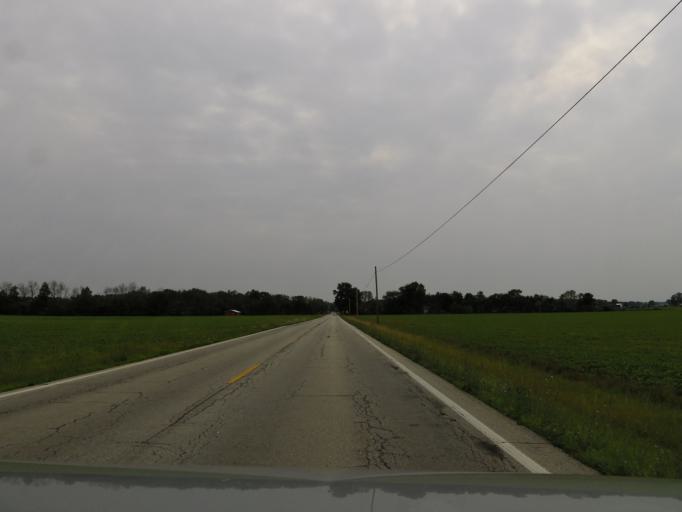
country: US
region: Ohio
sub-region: Clinton County
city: Blanchester
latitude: 39.3158
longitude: -83.9055
